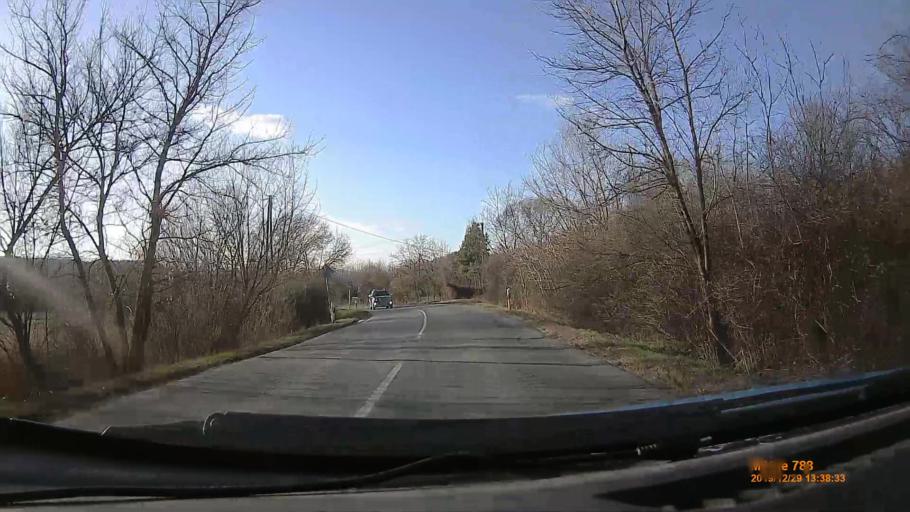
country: HU
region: Heves
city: Recsk
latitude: 47.9259
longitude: 20.1502
